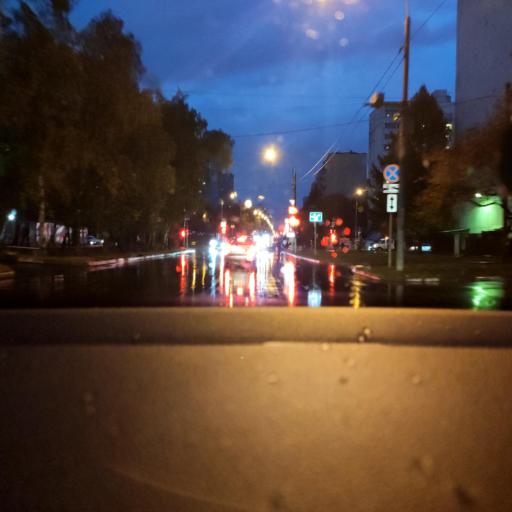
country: RU
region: Moskovskaya
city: Razvilka
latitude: 55.6033
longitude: 37.7355
